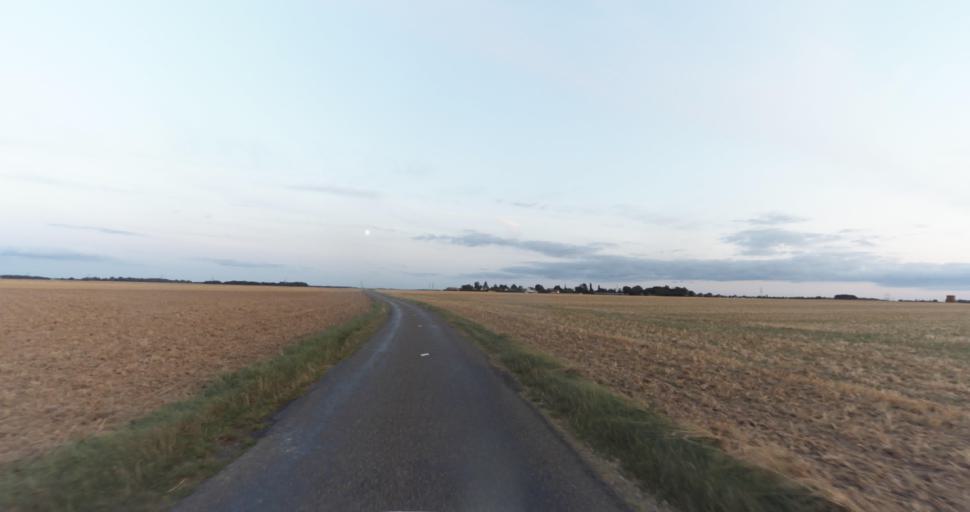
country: FR
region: Haute-Normandie
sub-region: Departement de l'Eure
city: La Madeleine-de-Nonancourt
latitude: 48.8755
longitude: 1.2446
